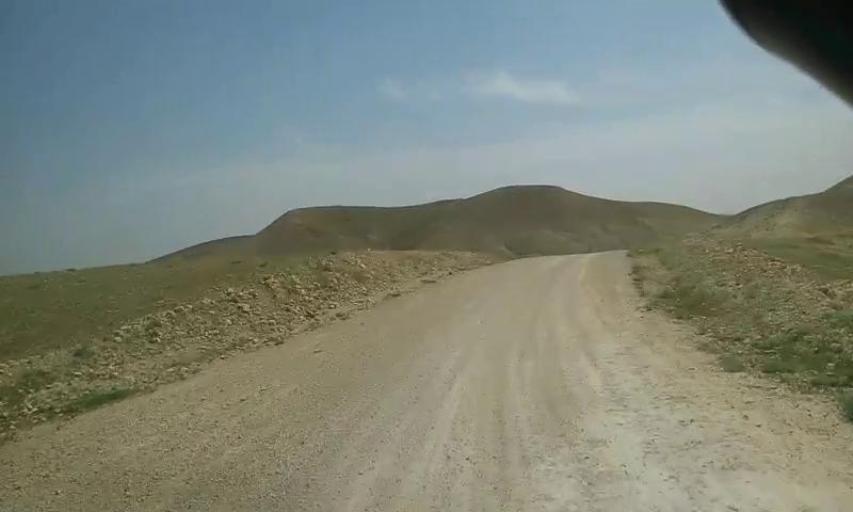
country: PS
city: `Arab ar Rashaydah
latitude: 31.4990
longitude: 35.2942
